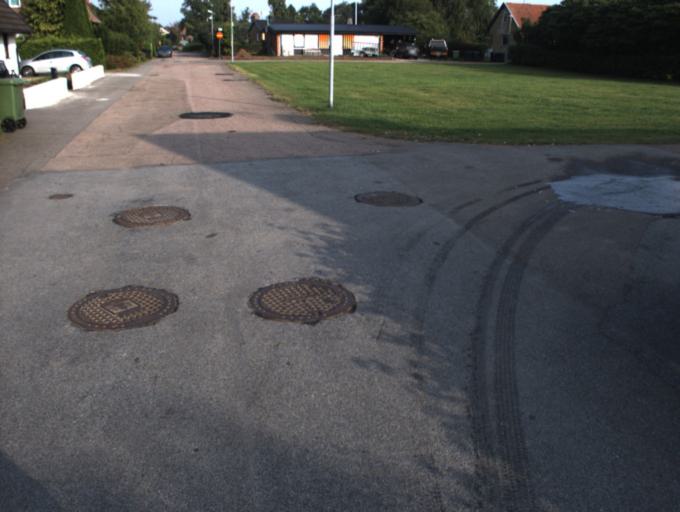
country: SE
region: Skane
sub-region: Angelholms Kommun
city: Strovelstorp
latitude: 56.1393
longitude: 12.7926
